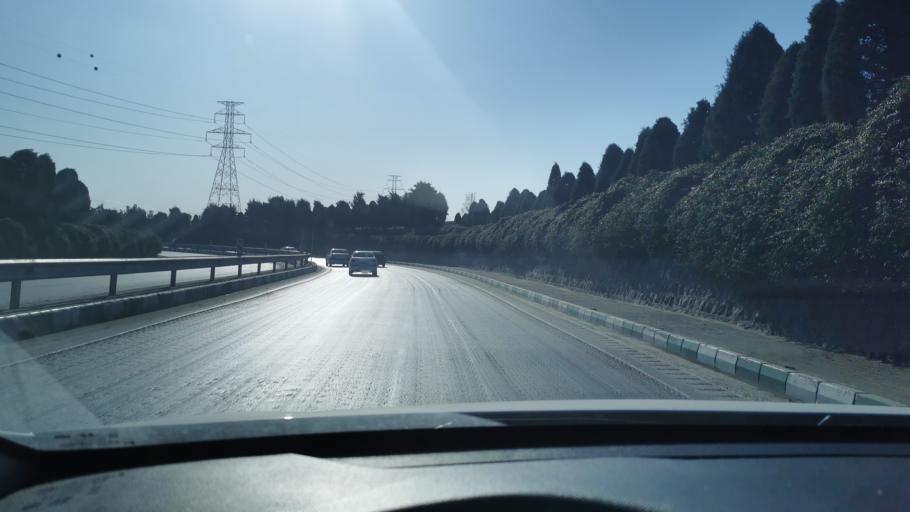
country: IR
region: Razavi Khorasan
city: Mashhad
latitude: 36.2628
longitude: 59.5809
